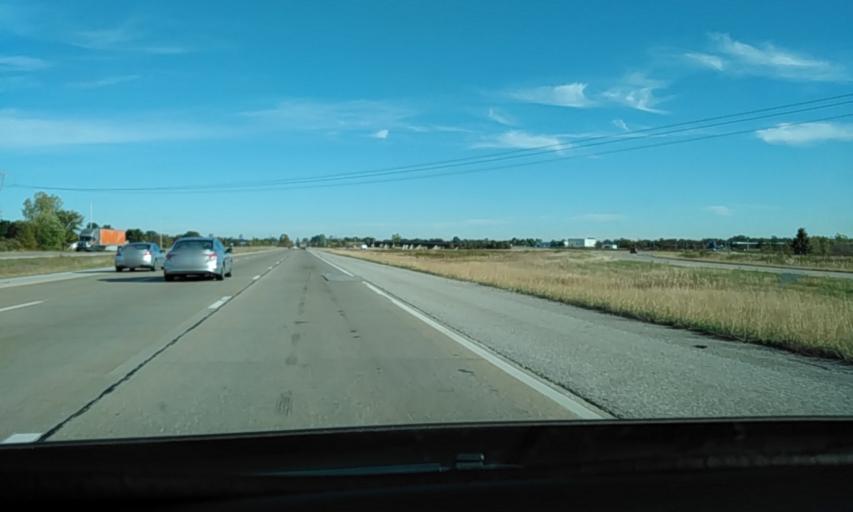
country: US
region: Illinois
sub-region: Saint Clair County
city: Dupo
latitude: 38.5218
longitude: -90.1992
